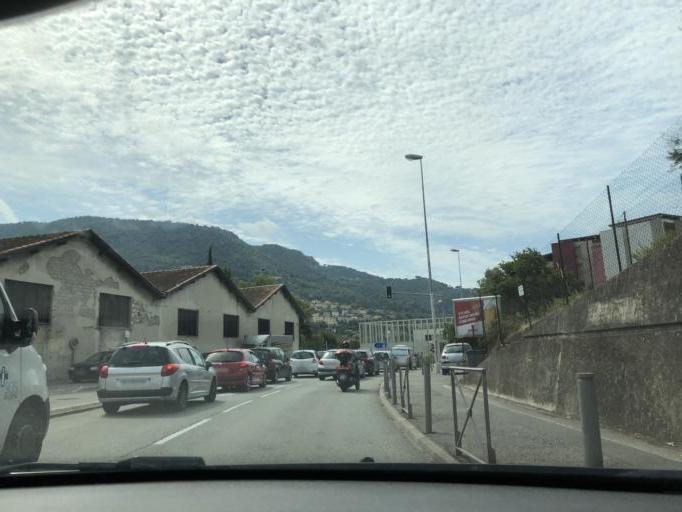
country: FR
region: Provence-Alpes-Cote d'Azur
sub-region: Departement des Alpes-Maritimes
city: La Trinite
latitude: 43.7417
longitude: 7.3089
